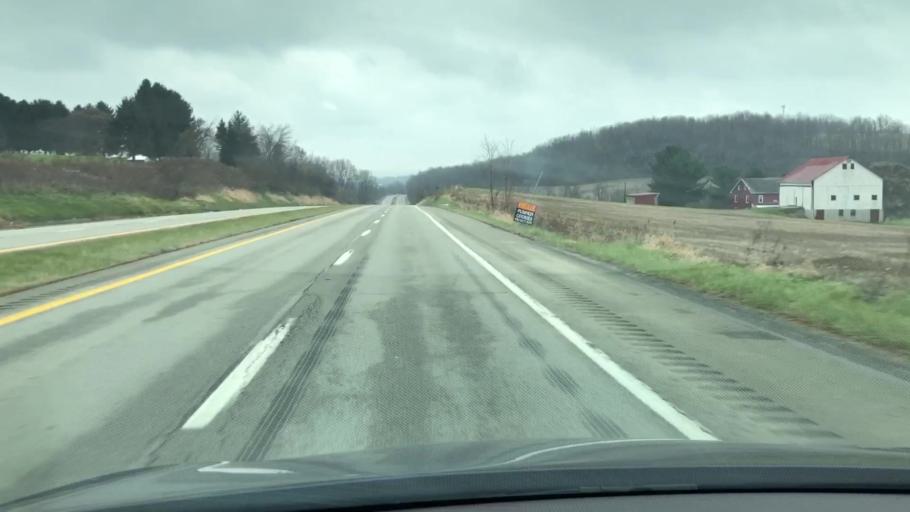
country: US
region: Pennsylvania
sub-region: Westmoreland County
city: Scottdale
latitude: 40.0859
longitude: -79.5602
